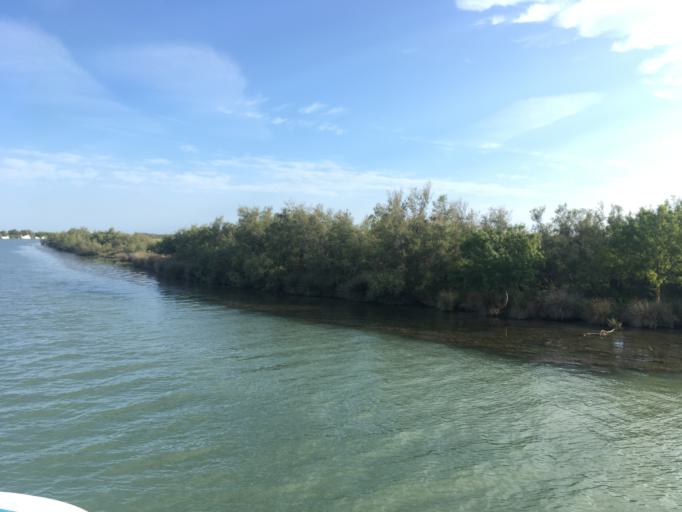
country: FR
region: Provence-Alpes-Cote d'Azur
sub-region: Departement des Bouches-du-Rhone
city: Saintes-Maries-de-la-Mer
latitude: 43.4744
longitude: 4.3913
